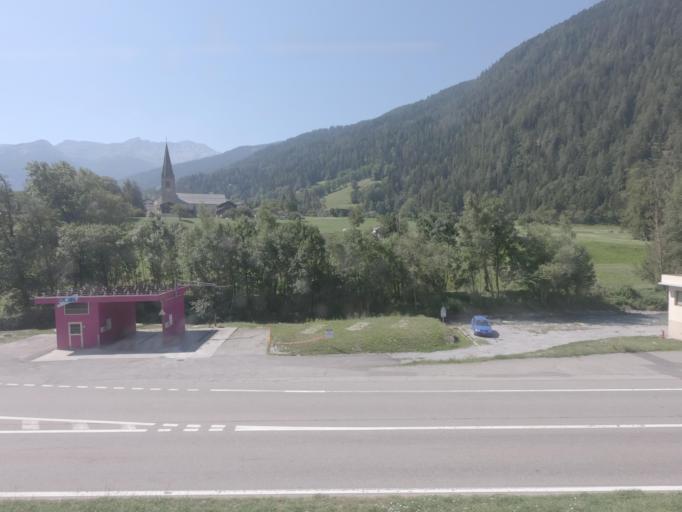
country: CH
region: Valais
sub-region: Entremont District
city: Bagnes
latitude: 46.0825
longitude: 7.2082
